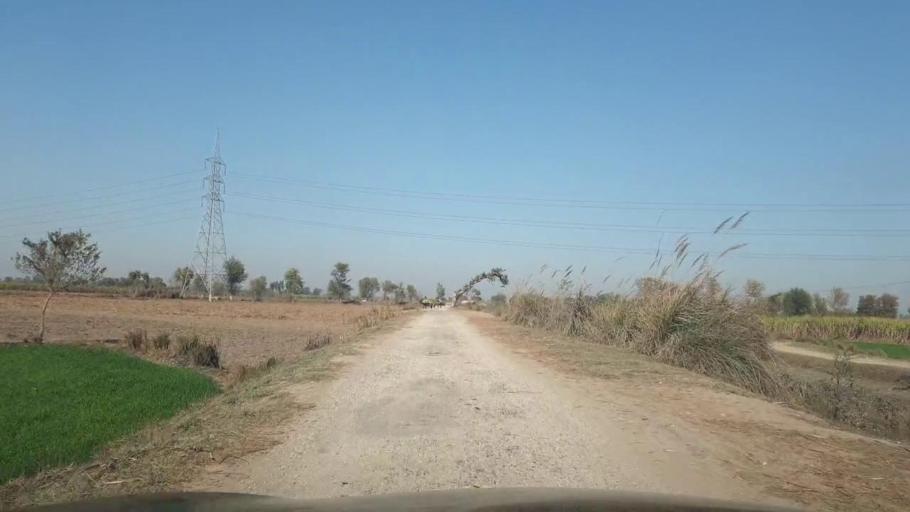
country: PK
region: Sindh
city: Ghotki
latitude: 27.9907
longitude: 69.4277
